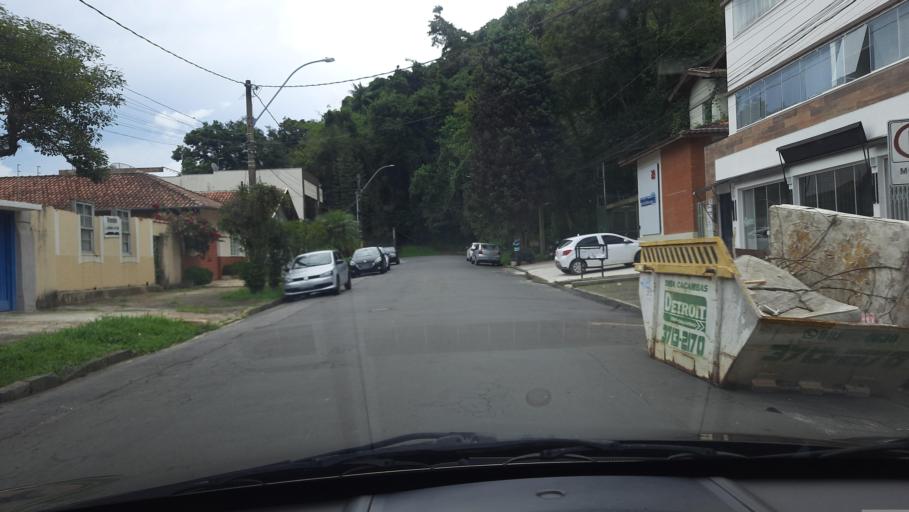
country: BR
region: Minas Gerais
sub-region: Pocos De Caldas
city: Pocos de Caldas
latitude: -21.7792
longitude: -46.5657
